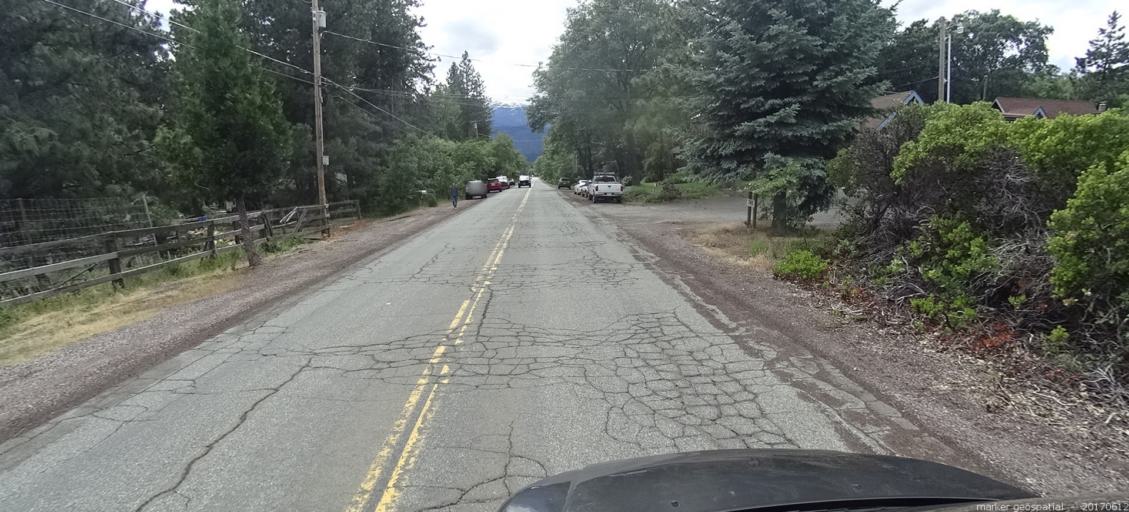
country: US
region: California
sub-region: Siskiyou County
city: Mount Shasta
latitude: 41.3271
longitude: -122.3079
